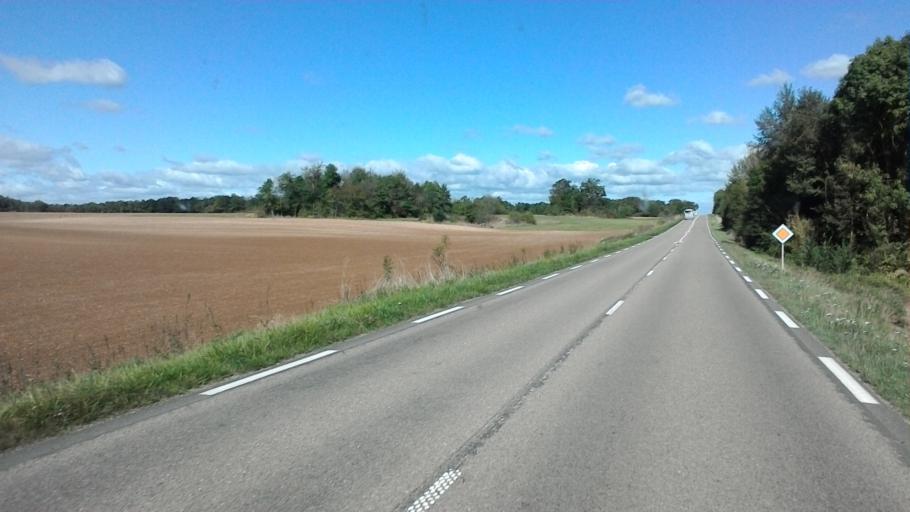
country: FR
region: Lorraine
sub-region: Departement des Vosges
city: Neufchateau
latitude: 48.3902
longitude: 5.7222
